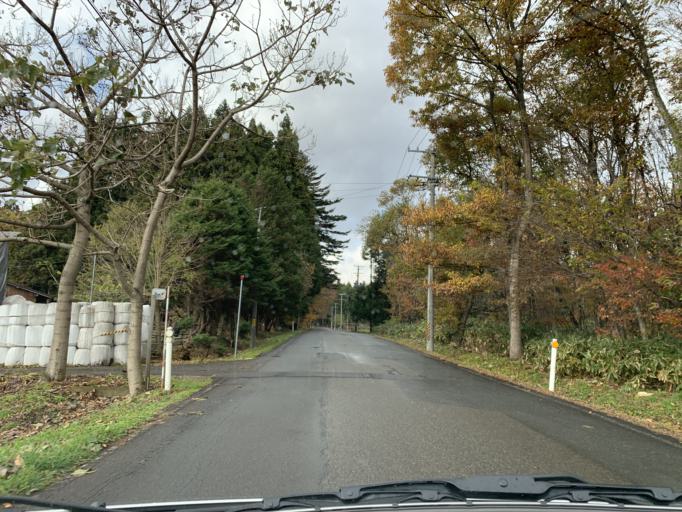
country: JP
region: Iwate
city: Mizusawa
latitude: 39.1014
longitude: 140.9961
